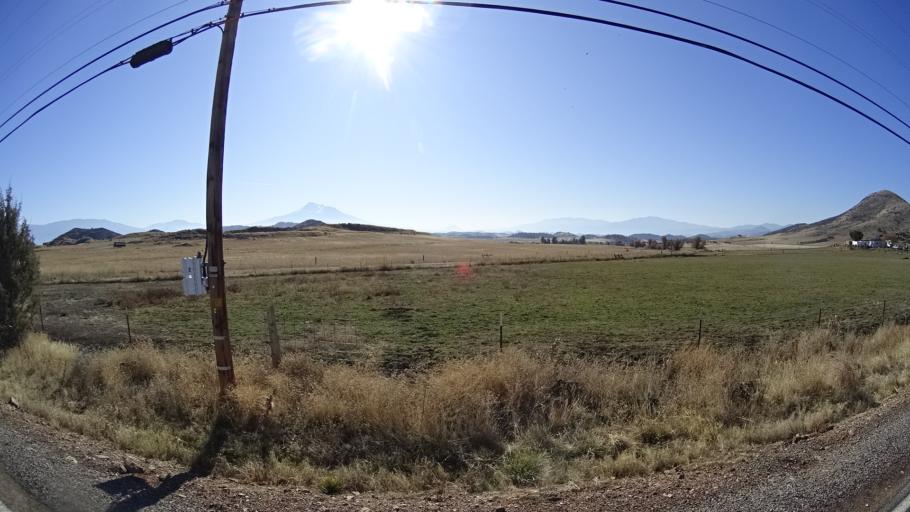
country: US
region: California
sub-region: Siskiyou County
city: Montague
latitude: 41.7267
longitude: -122.5011
